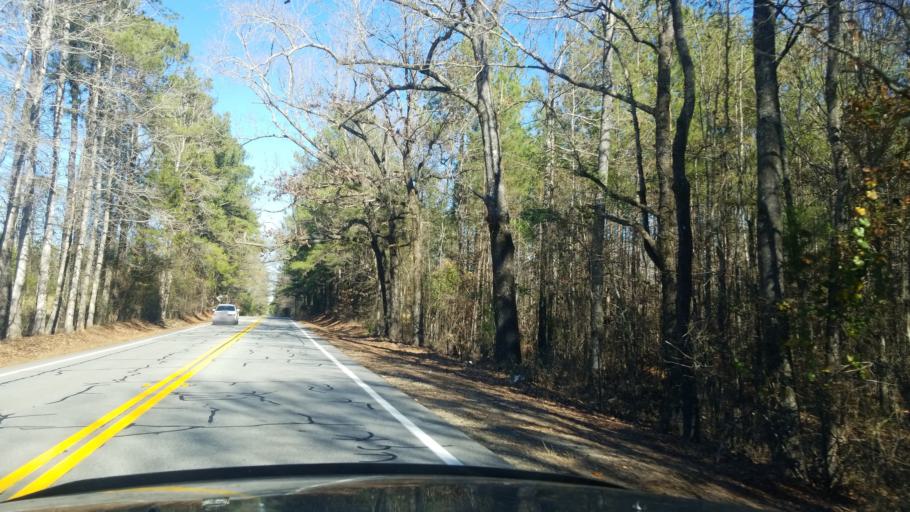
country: US
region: Georgia
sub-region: Harris County
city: Hamilton
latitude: 32.6783
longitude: -84.8589
